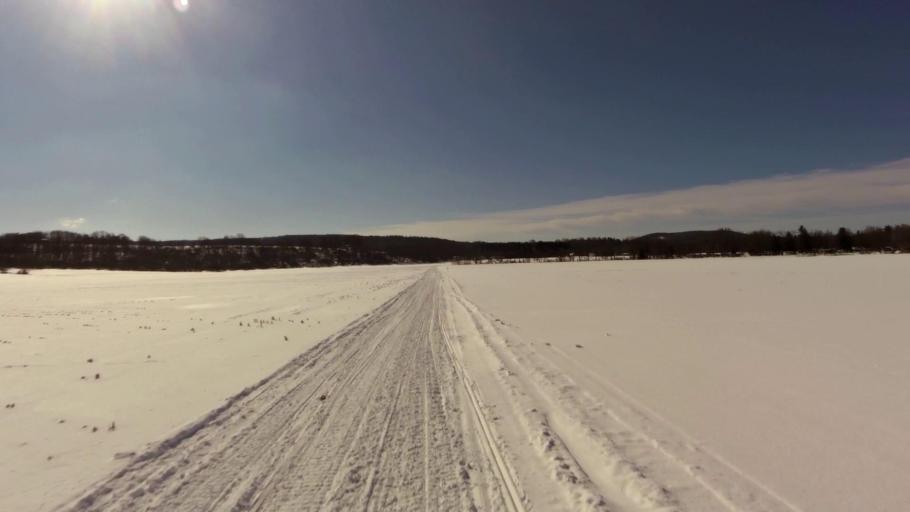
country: US
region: New York
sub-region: Cattaraugus County
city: Franklinville
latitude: 42.3529
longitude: -78.4508
